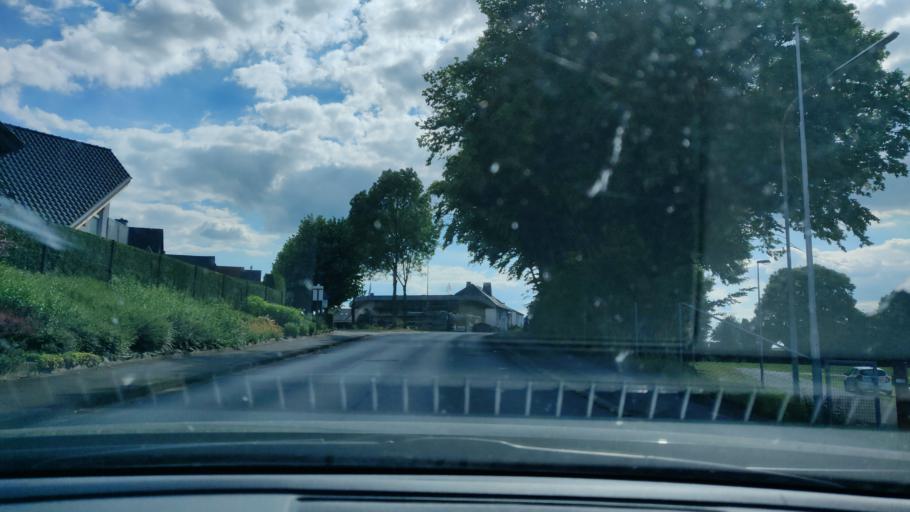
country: DE
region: Hesse
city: Gudensberg
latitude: 51.1768
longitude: 9.3586
